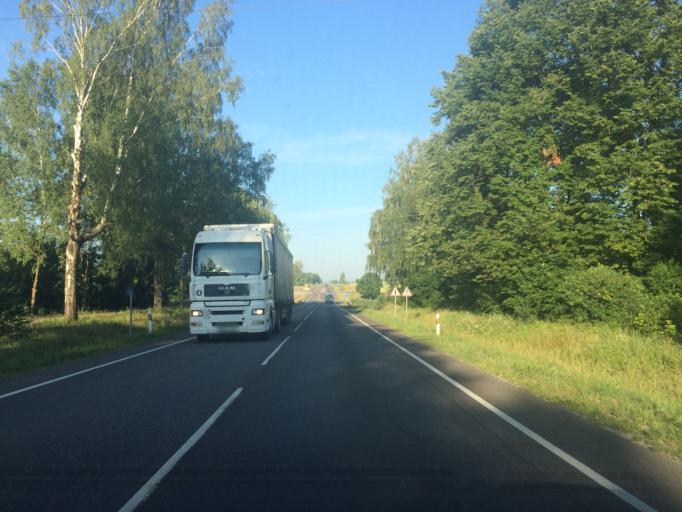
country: LT
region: Vilnius County
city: Ukmerge
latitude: 55.2364
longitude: 24.7270
